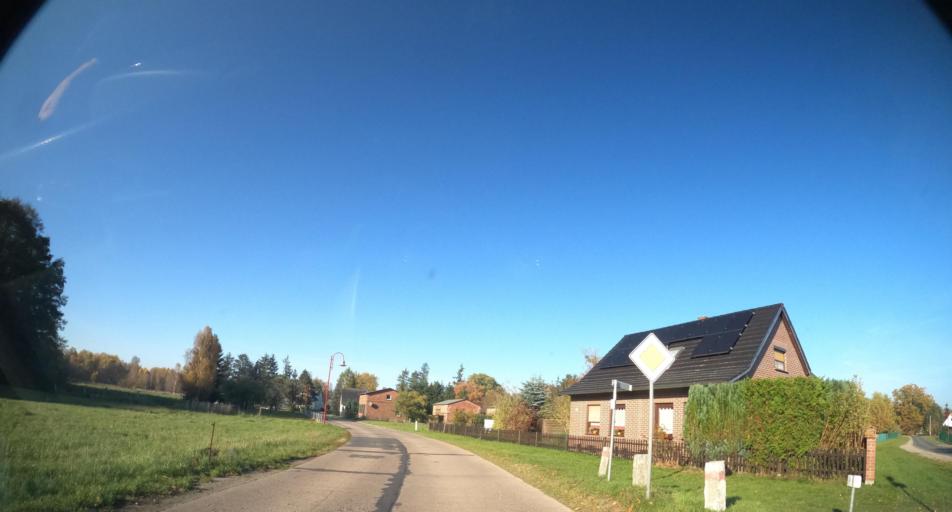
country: DE
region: Mecklenburg-Vorpommern
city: Ahlbeck
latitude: 53.6243
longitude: 14.2640
